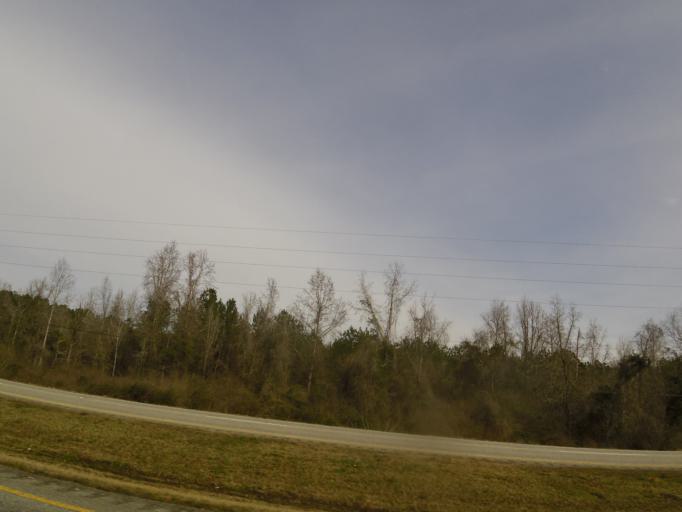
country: US
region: Alabama
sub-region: Dale County
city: Ozark
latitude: 31.4535
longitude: -85.6633
